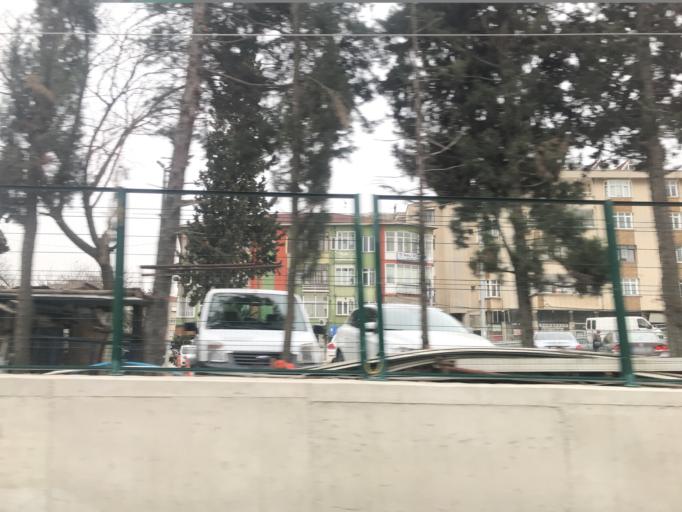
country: TR
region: Istanbul
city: Pendik
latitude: 40.8798
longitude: 29.2276
